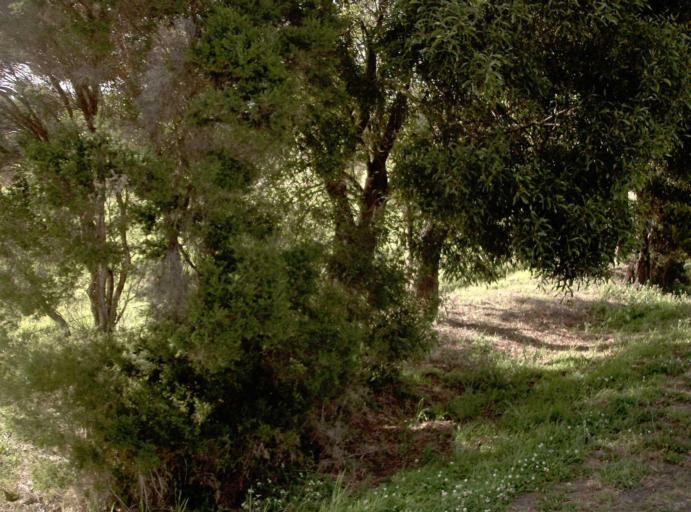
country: AU
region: Victoria
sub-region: Cardinia
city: Bunyip
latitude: -38.0852
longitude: 145.7777
